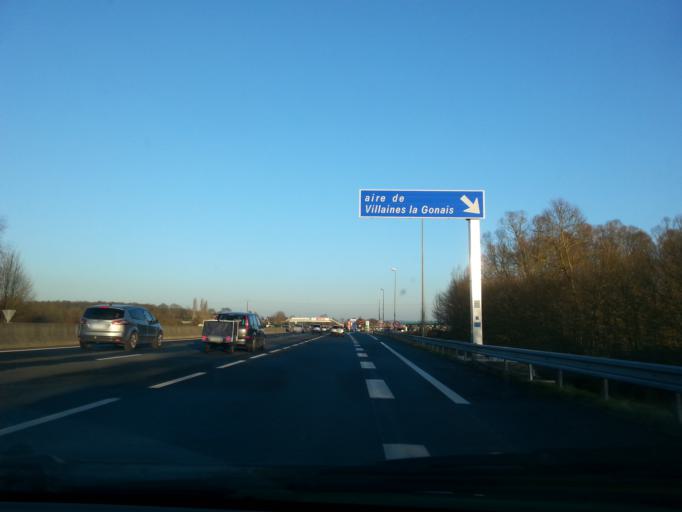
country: FR
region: Pays de la Loire
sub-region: Departement de la Sarthe
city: Le Luart
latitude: 48.1239
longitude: 0.6174
